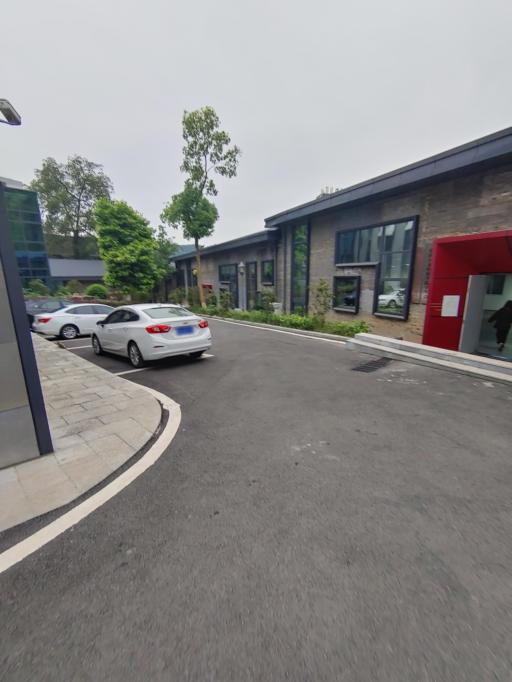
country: CN
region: Chongqing Shi
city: Shuangfeng
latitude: 29.9731
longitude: 106.4122
